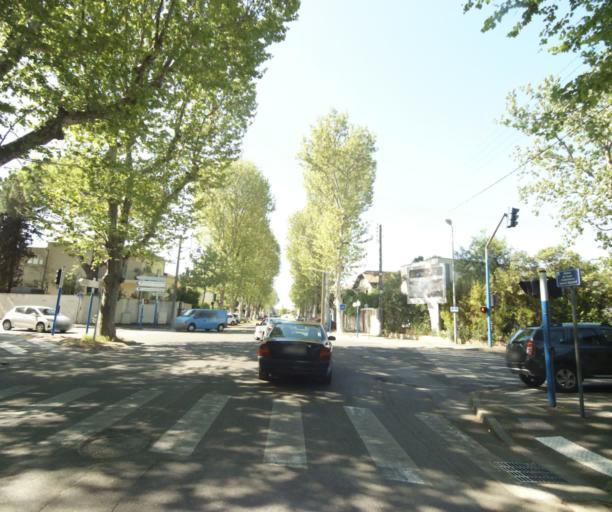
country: FR
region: Languedoc-Roussillon
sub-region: Departement de l'Herault
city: Montpellier
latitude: 43.6155
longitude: 3.8564
